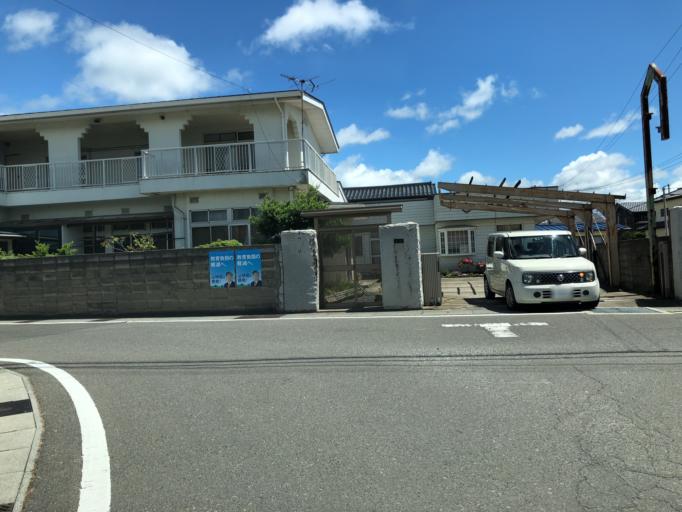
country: JP
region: Fukushima
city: Fukushima-shi
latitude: 37.8076
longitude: 140.4405
